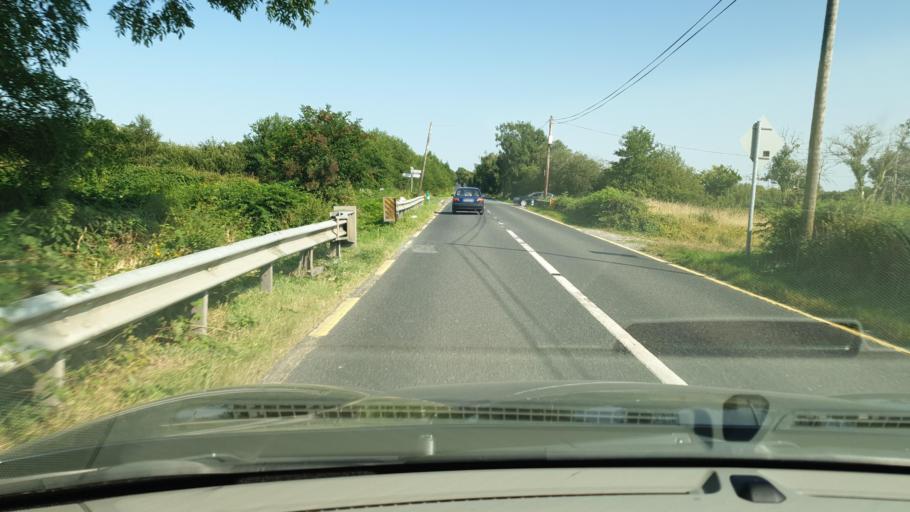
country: IE
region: Leinster
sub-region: An Mhi
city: Trim
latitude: 53.6337
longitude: -6.8123
